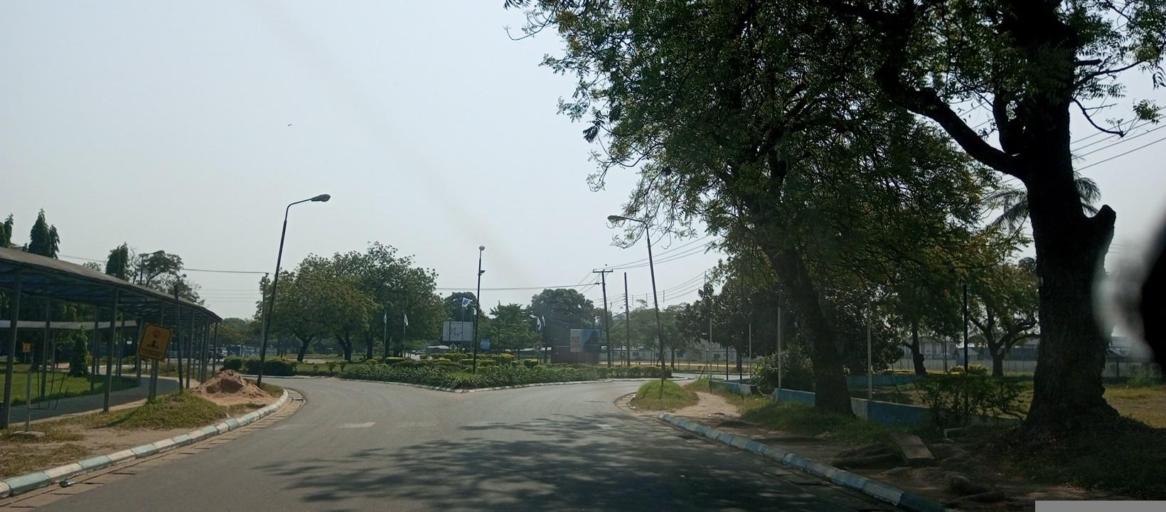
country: NG
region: Rivers
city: Emuoha
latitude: 4.9031
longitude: 6.9198
